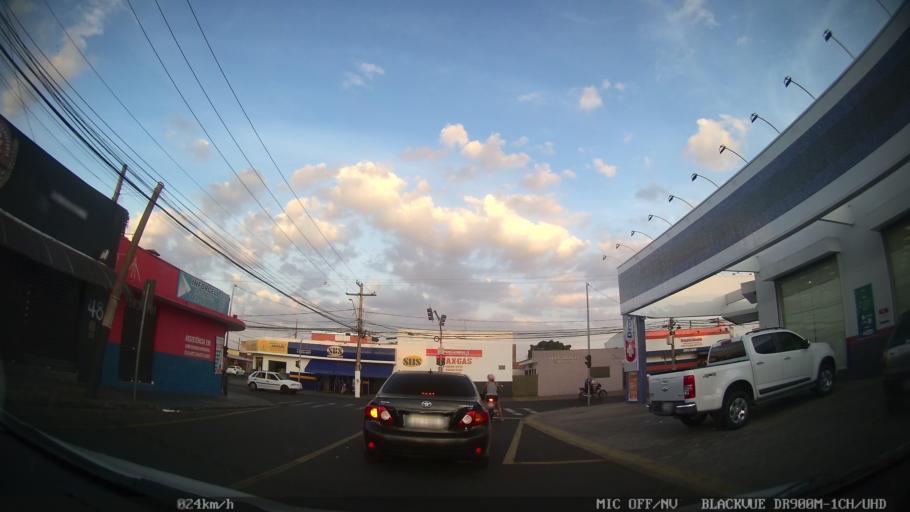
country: BR
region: Sao Paulo
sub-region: Ribeirao Preto
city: Ribeirao Preto
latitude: -21.1275
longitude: -47.8112
